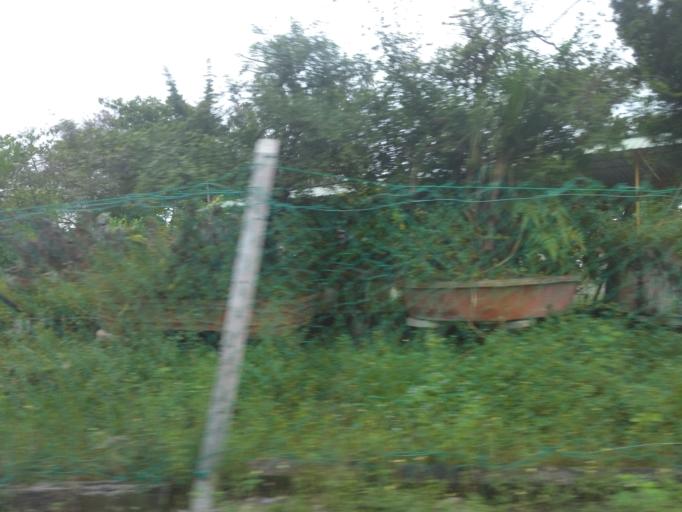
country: MY
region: Penang
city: Bukit Mertajam
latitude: 5.3362
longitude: 100.4796
